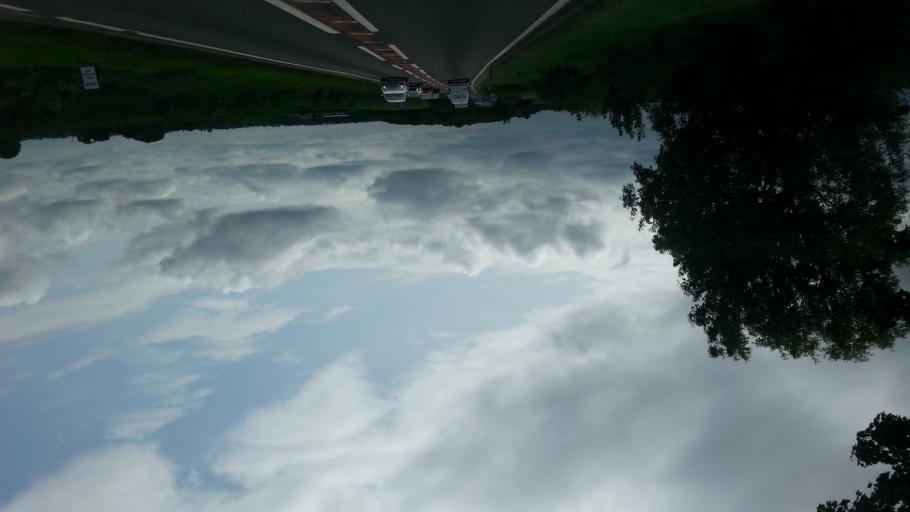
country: GB
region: England
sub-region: Northamptonshire
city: Northampton
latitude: 52.3001
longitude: -0.8271
